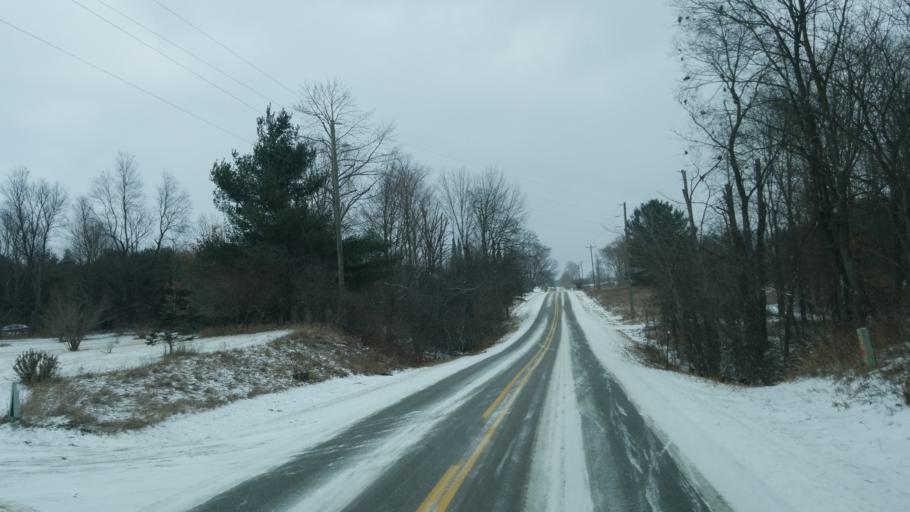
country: US
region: Michigan
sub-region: Osceola County
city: Reed City
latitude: 43.8218
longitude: -85.4100
